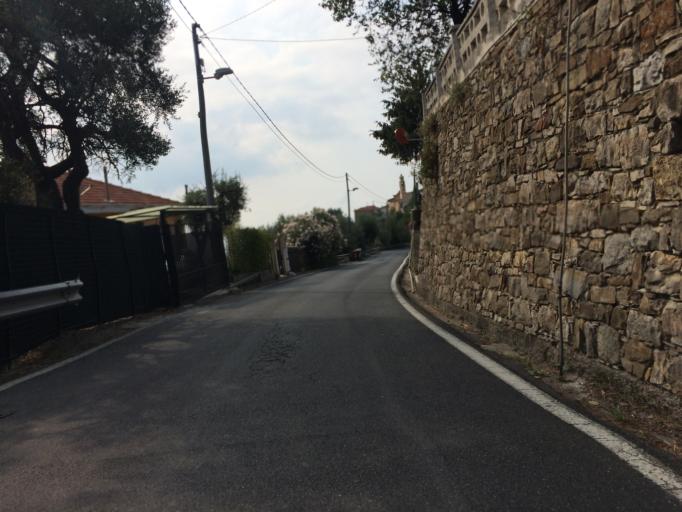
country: IT
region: Liguria
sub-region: Provincia di Imperia
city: San Remo
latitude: 43.8361
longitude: 7.7577
